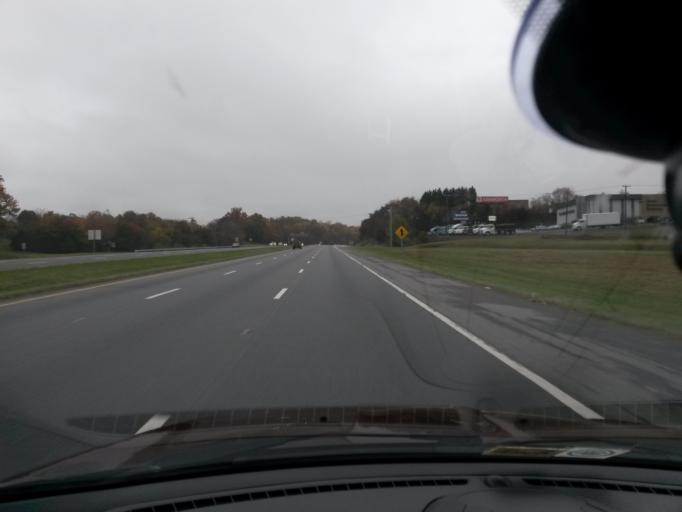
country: US
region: Virginia
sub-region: Roanoke County
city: Hollins
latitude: 37.3284
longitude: -79.9898
